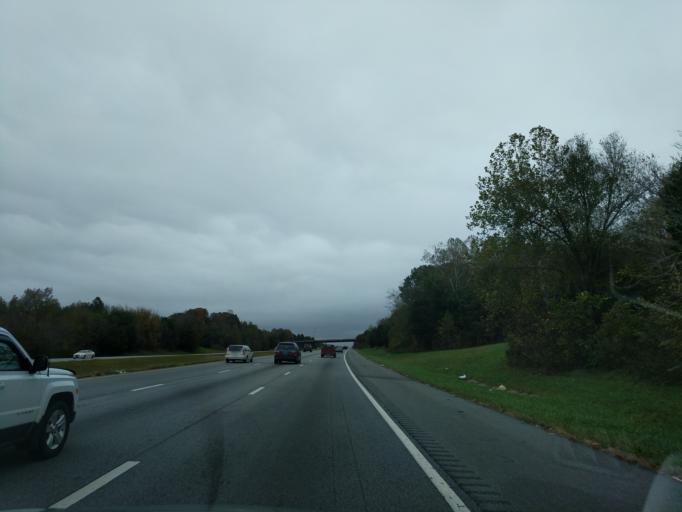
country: US
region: North Carolina
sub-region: Randolph County
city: Trinity
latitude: 35.8840
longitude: -79.9956
